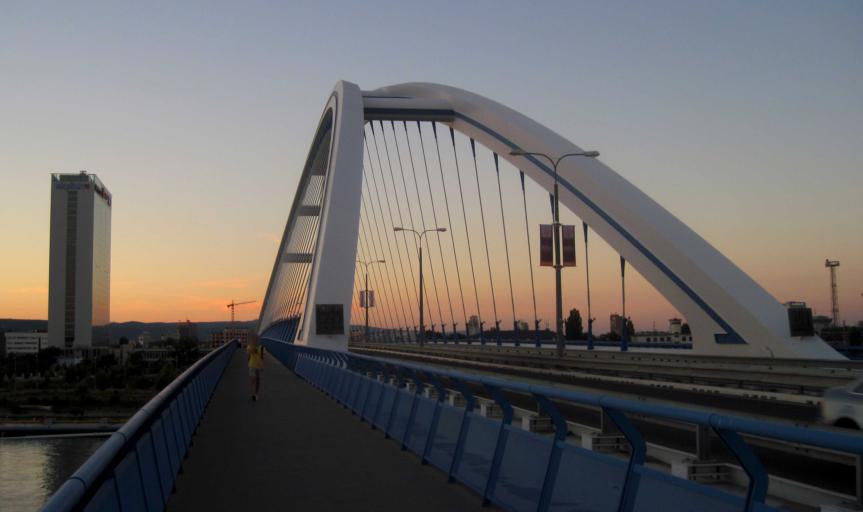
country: SK
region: Bratislavsky
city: Bratislava
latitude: 48.1360
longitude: 17.1277
